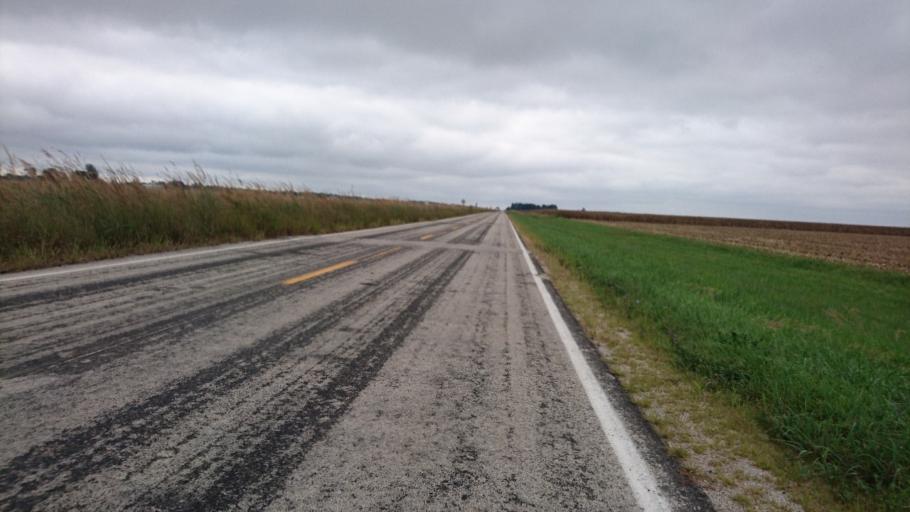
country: US
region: Illinois
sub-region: Montgomery County
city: Raymond
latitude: 39.3165
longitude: -89.6431
